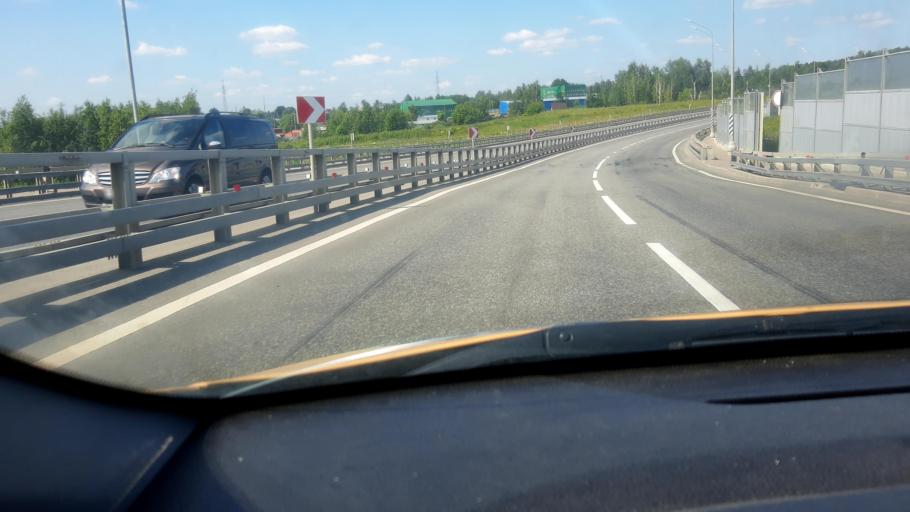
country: RU
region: Moskovskaya
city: Kokoshkino
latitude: 55.5935
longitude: 37.1502
